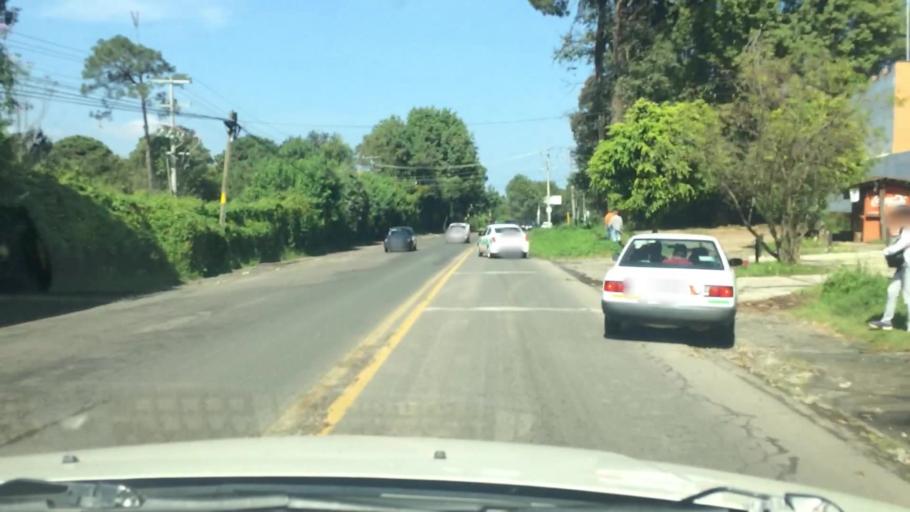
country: MX
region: Mexico
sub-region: Valle de Bravo
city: Casas Viejas
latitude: 19.1594
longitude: -100.0999
